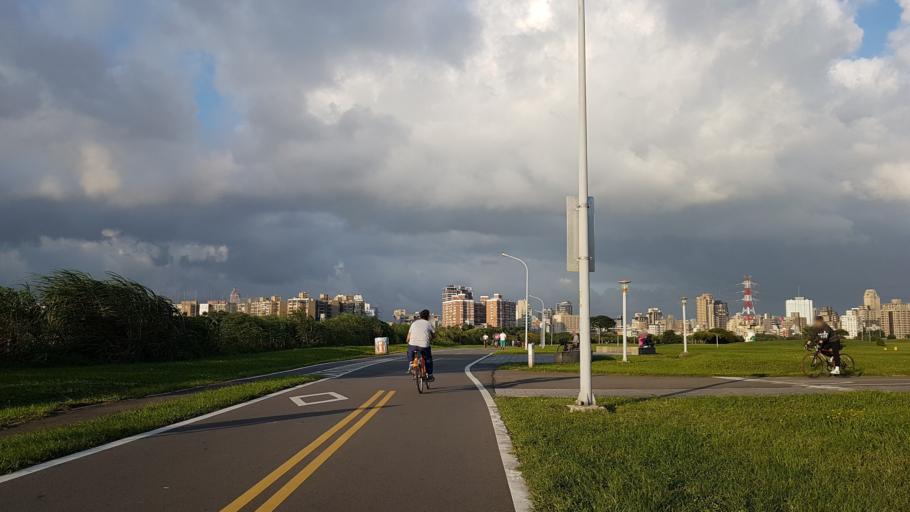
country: TW
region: Taipei
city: Taipei
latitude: 25.0181
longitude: 121.5065
